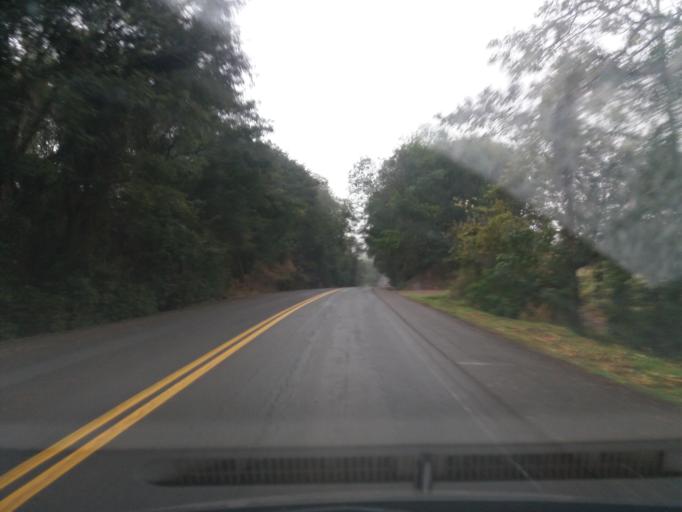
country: BR
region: Parana
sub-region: Ampere
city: Ampere
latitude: -25.8611
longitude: -53.4949
